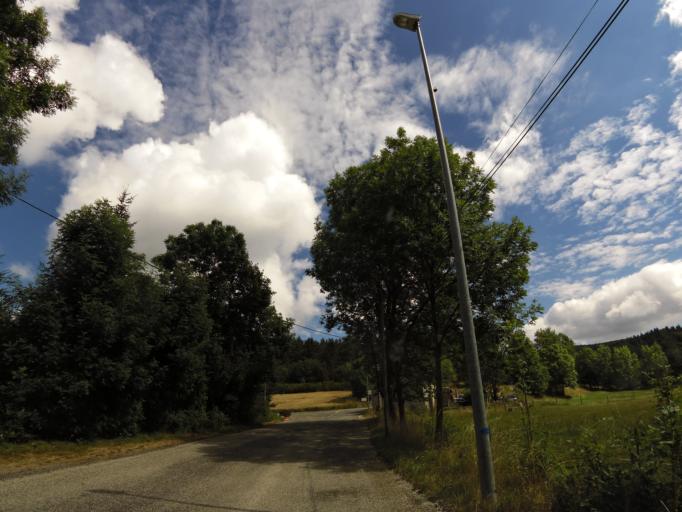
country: FR
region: Languedoc-Roussillon
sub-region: Departement de la Lozere
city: Meyrueis
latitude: 44.1116
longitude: 3.4821
